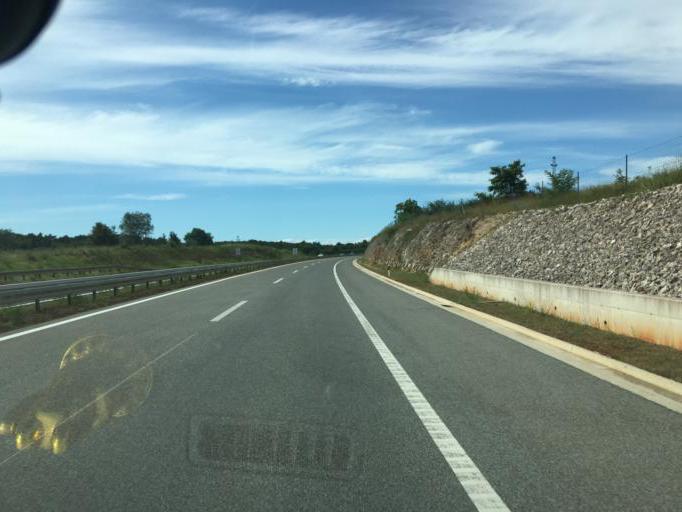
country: HR
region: Istarska
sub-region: Grad Rovinj
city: Rovinj
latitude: 45.1288
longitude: 13.7721
